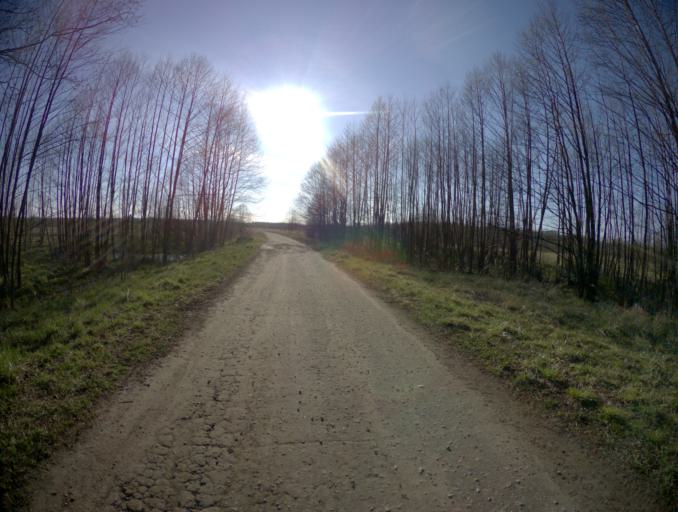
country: RU
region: Vladimir
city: Ivanishchi
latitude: 55.6481
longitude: 40.3908
